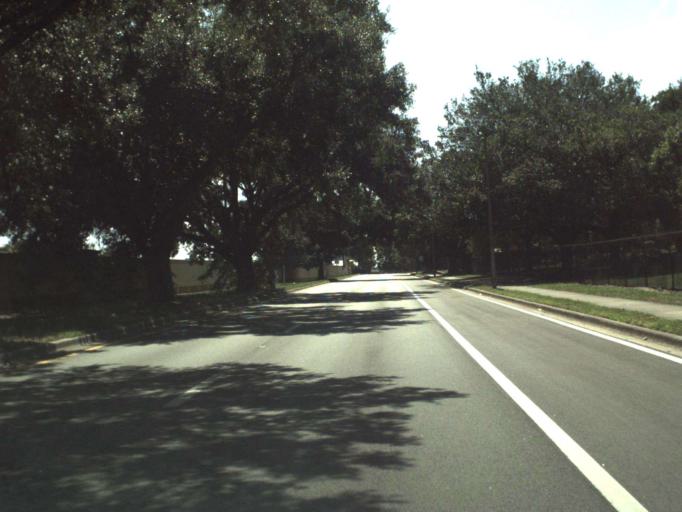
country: US
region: Florida
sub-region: Orange County
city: Orlando
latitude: 28.5378
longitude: -81.3576
